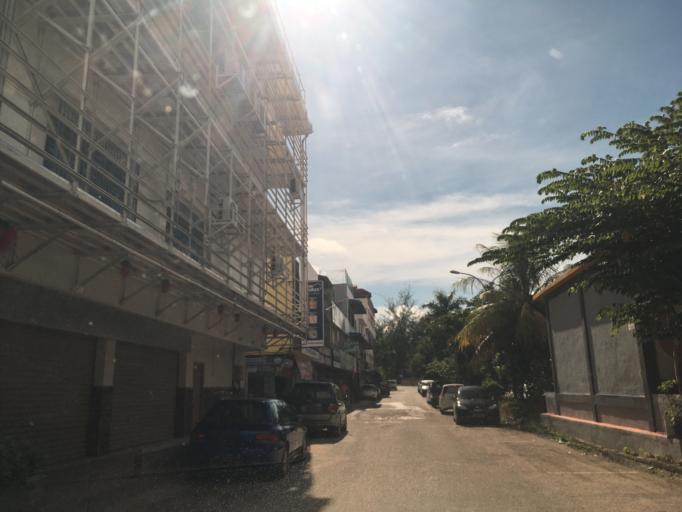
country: SG
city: Singapore
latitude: 1.1498
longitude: 104.0108
